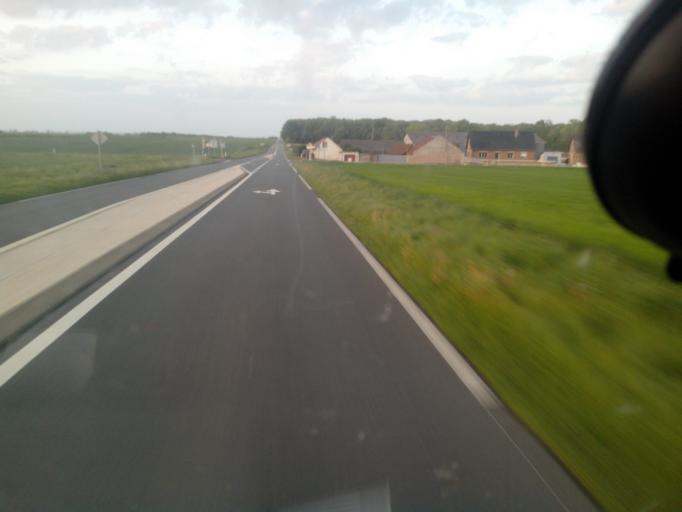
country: FR
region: Picardie
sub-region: Departement de la Somme
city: Crecy-en-Ponthieu
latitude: 50.2125
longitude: 1.9099
